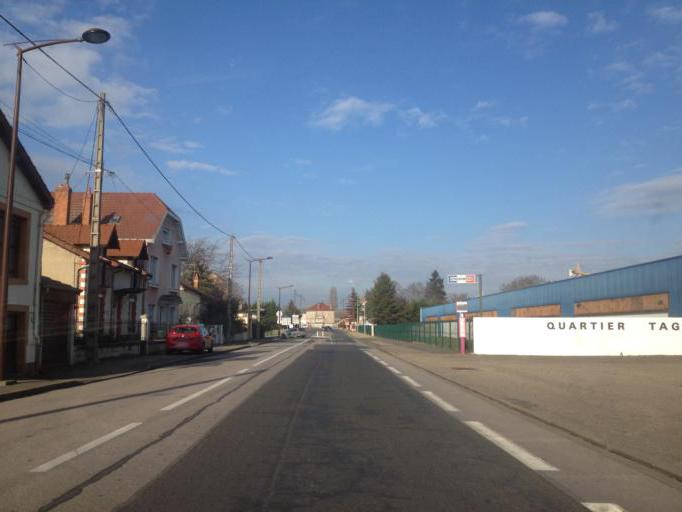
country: FR
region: Auvergne
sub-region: Departement de l'Allier
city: Moulins
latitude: 46.5771
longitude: 3.3243
